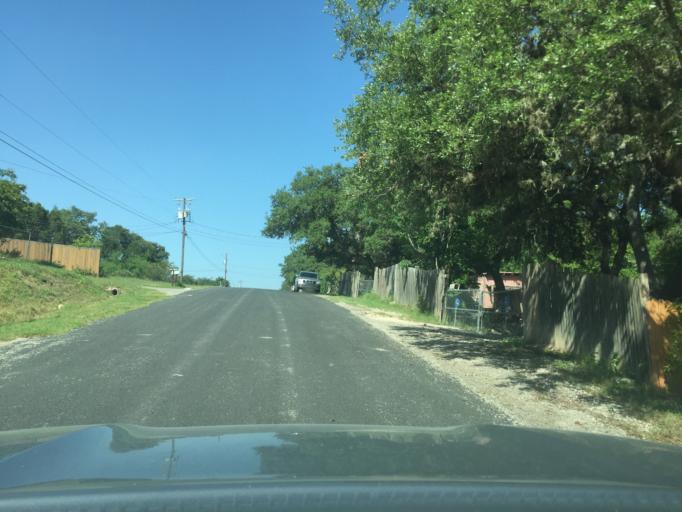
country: US
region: Texas
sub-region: Bexar County
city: Timberwood Park
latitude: 29.7074
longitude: -98.4727
